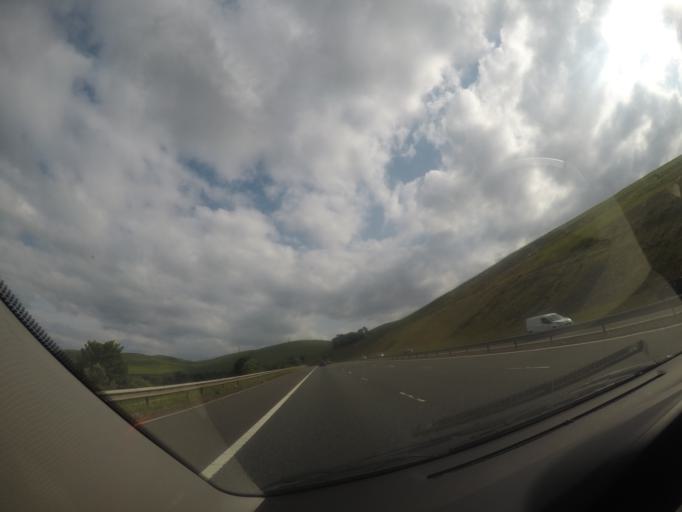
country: GB
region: Scotland
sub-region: South Lanarkshire
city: Douglas
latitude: 55.4770
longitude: -3.6955
